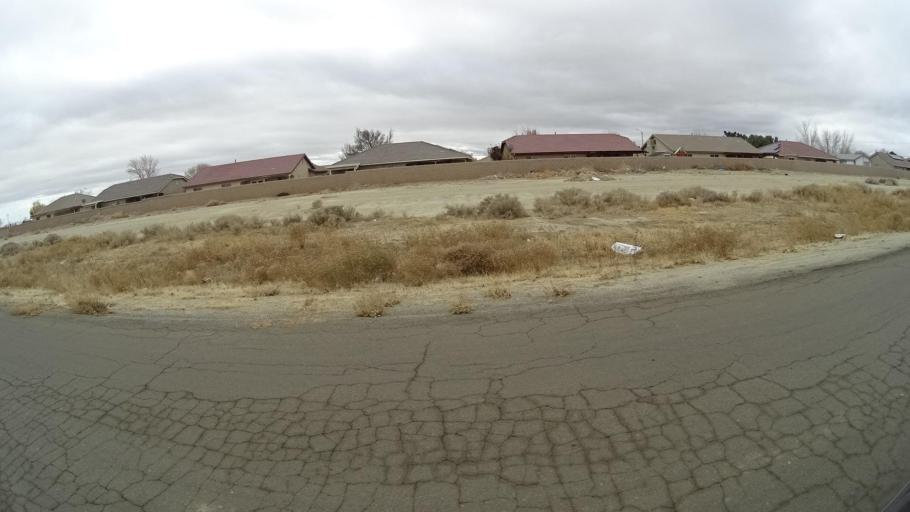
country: US
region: California
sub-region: Kern County
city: Rosamond
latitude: 34.8499
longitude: -118.1654
